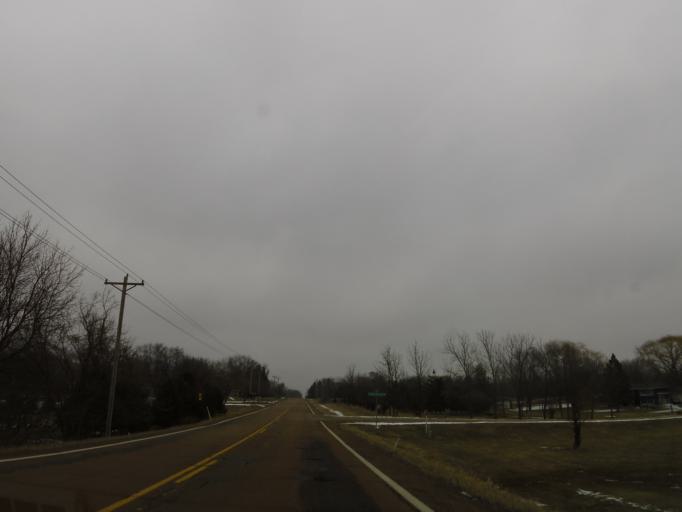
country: US
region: Minnesota
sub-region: Scott County
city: Prior Lake
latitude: 44.6824
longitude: -93.4606
